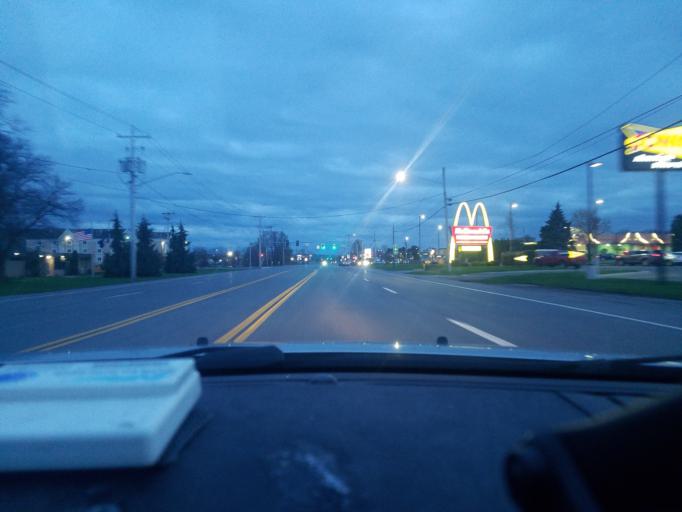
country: US
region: New York
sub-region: Onondaga County
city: North Syracuse
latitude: 43.1197
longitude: -76.1422
